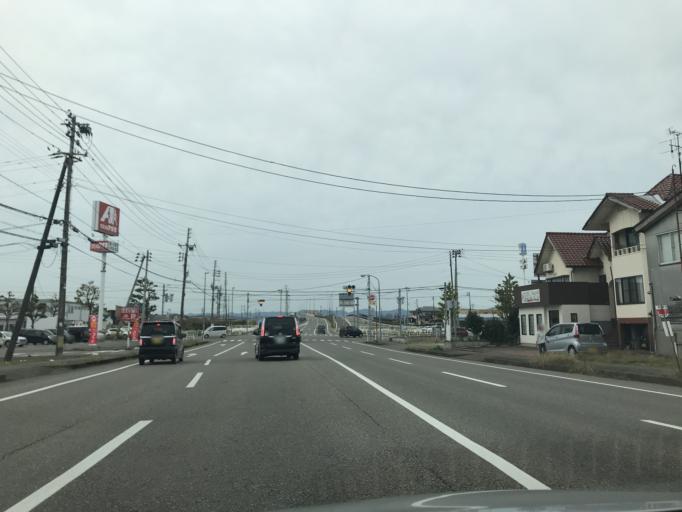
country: JP
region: Niigata
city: Nagaoka
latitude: 37.4269
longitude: 138.8367
